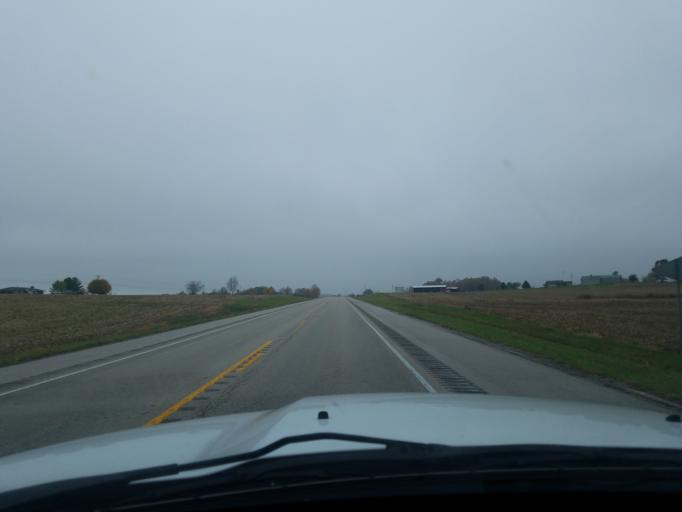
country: US
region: Kentucky
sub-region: Green County
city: Greensburg
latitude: 37.4142
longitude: -85.4963
